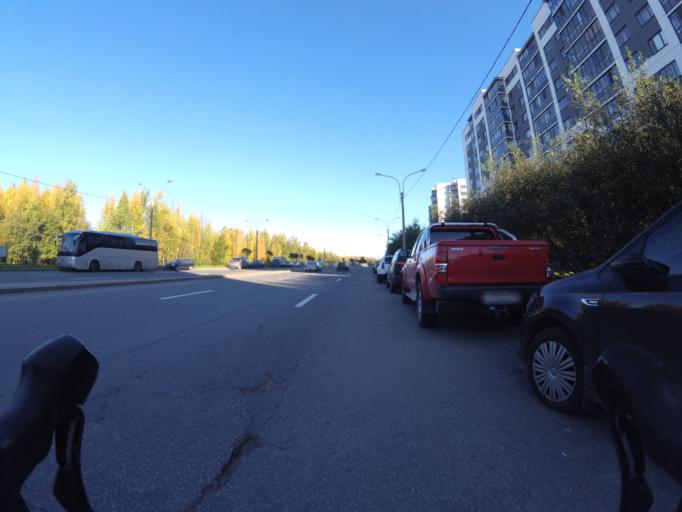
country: RU
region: Leningrad
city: Untolovo
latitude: 60.0068
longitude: 30.1985
